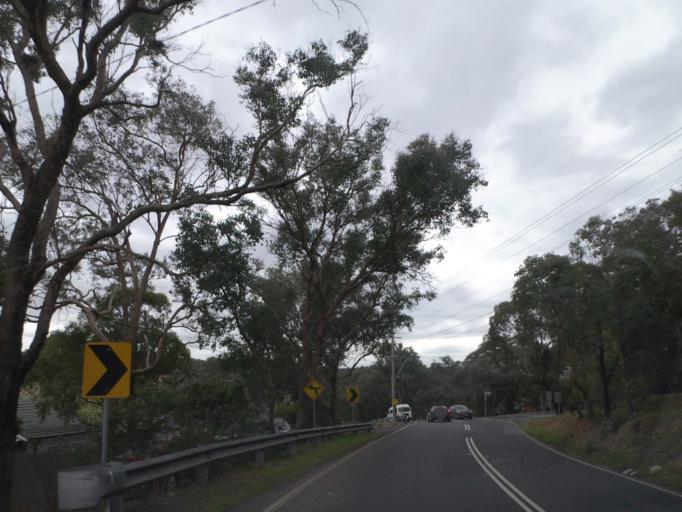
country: AU
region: Victoria
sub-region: Nillumbik
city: Diamond Creek
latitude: -37.6781
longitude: 145.1441
